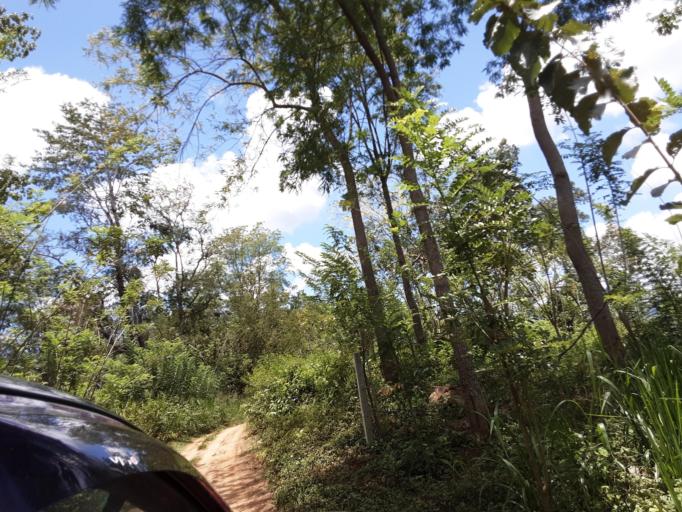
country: LK
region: Uva
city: Haputale
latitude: 6.8209
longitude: 81.1097
